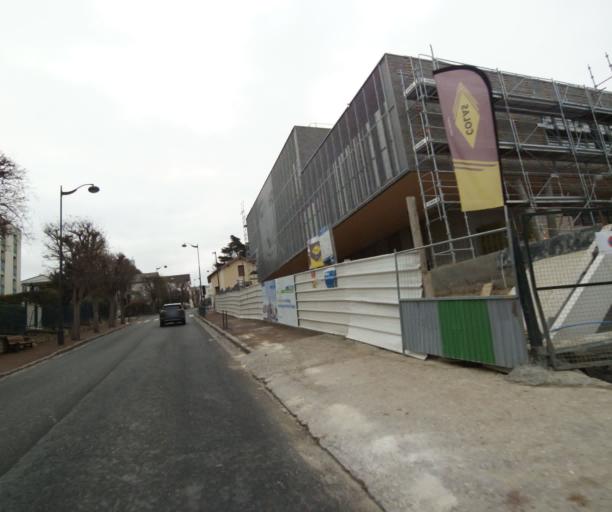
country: FR
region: Ile-de-France
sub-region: Departement des Hauts-de-Seine
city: Rueil-Malmaison
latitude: 48.8756
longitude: 2.1868
